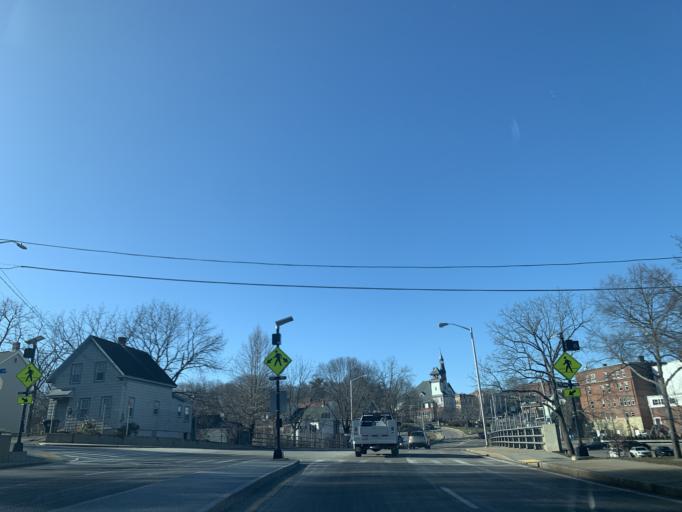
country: US
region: Massachusetts
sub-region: Middlesex County
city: Marlborough
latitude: 42.3455
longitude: -71.5512
